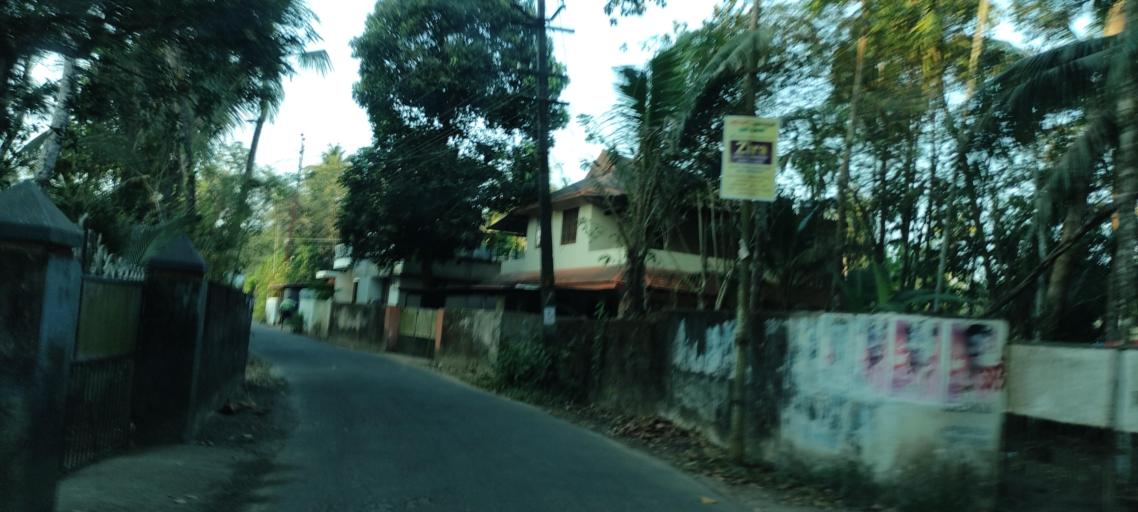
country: IN
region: Kerala
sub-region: Alappuzha
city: Kutiatodu
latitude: 9.7750
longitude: 76.3254
